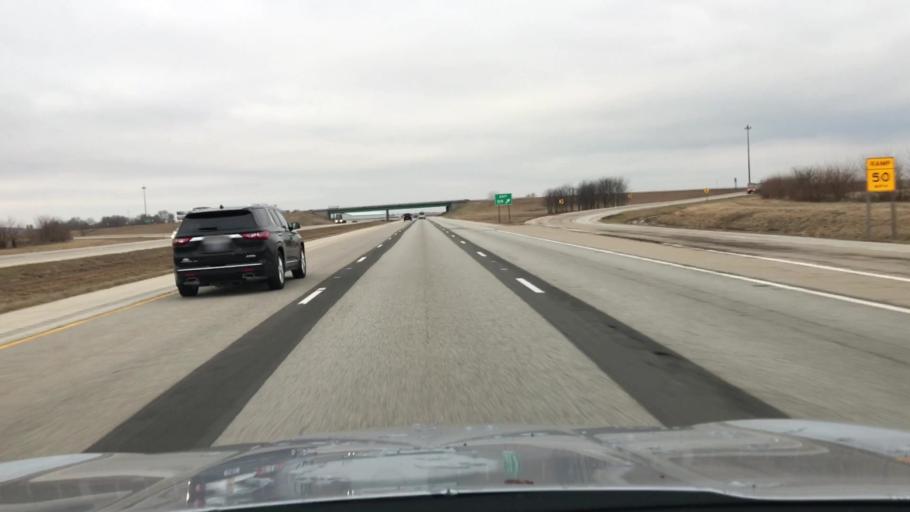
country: US
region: Illinois
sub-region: Logan County
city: Lincoln
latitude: 40.0770
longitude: -89.4385
